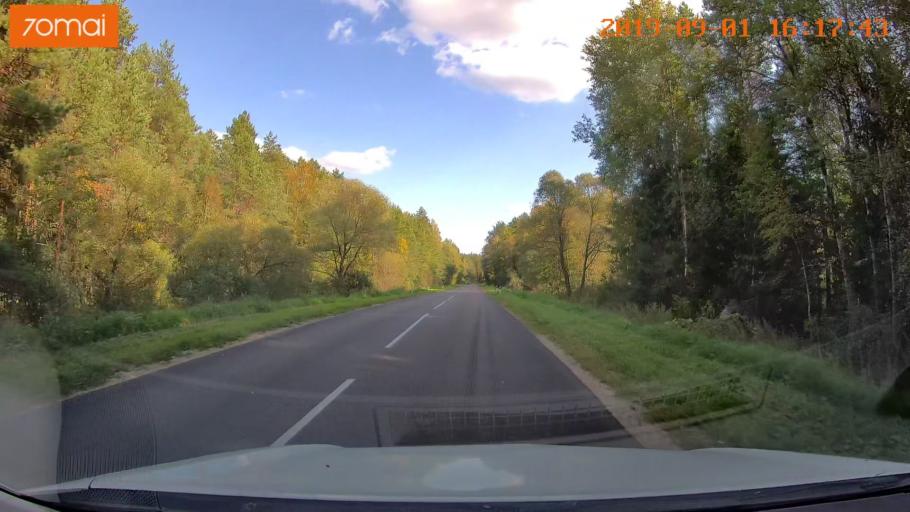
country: RU
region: Kaluga
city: Maloyaroslavets
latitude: 54.9063
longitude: 36.5109
